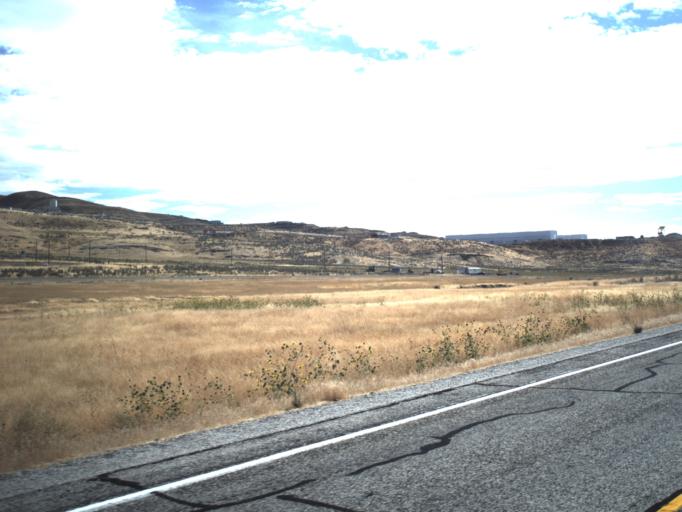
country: US
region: Utah
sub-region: Box Elder County
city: Tremonton
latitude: 41.6876
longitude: -112.4441
